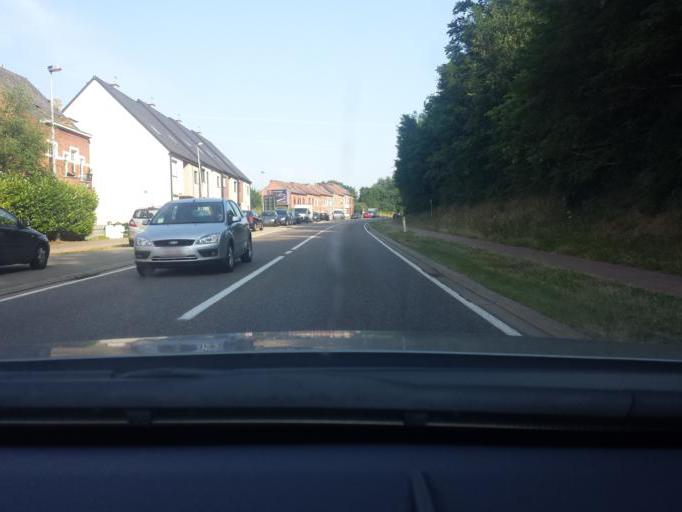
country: BE
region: Flanders
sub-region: Provincie Vlaams-Brabant
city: Diest
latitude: 50.9813
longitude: 5.0413
